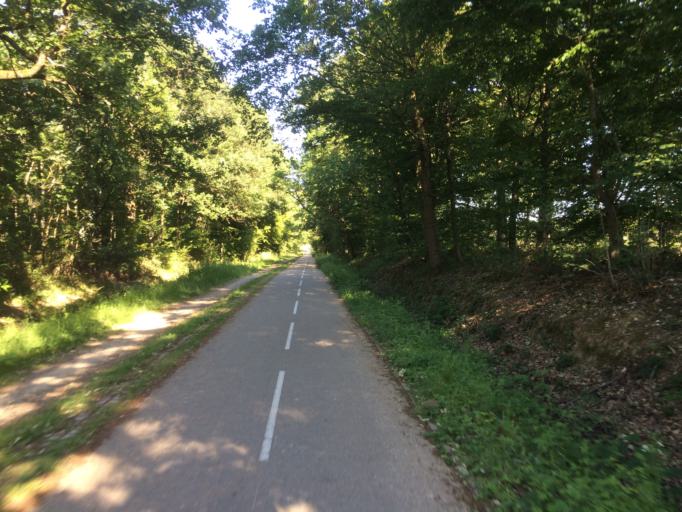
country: FR
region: Ile-de-France
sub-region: Departement du Val-de-Marne
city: Sucy-en-Brie
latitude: 48.7476
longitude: 2.5506
